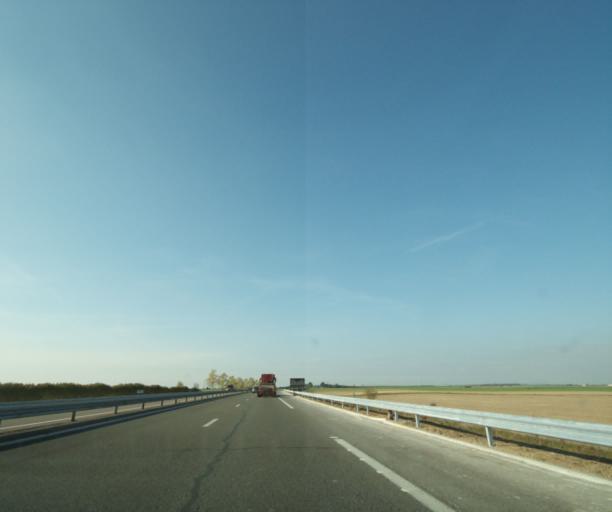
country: FR
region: Champagne-Ardenne
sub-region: Departement de la Marne
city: Saint-Memmie
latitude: 49.0338
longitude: 4.4010
